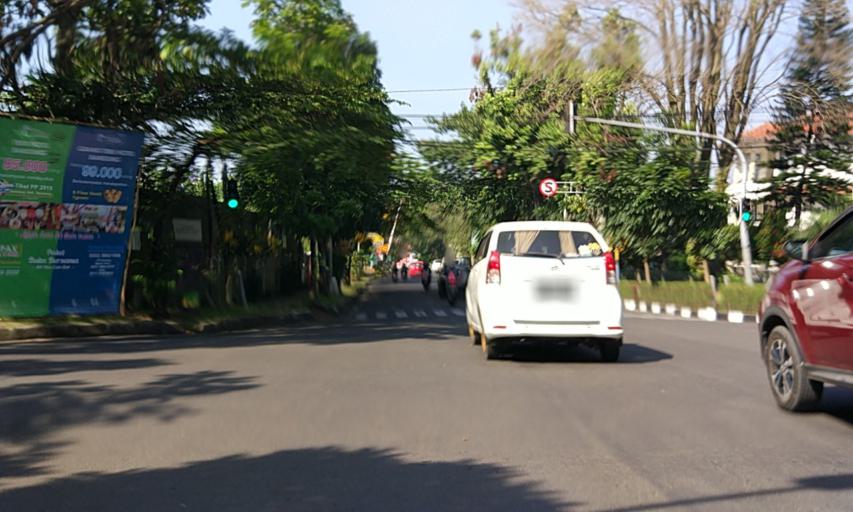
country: ID
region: West Java
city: Bandung
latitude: -6.9149
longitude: 107.6141
